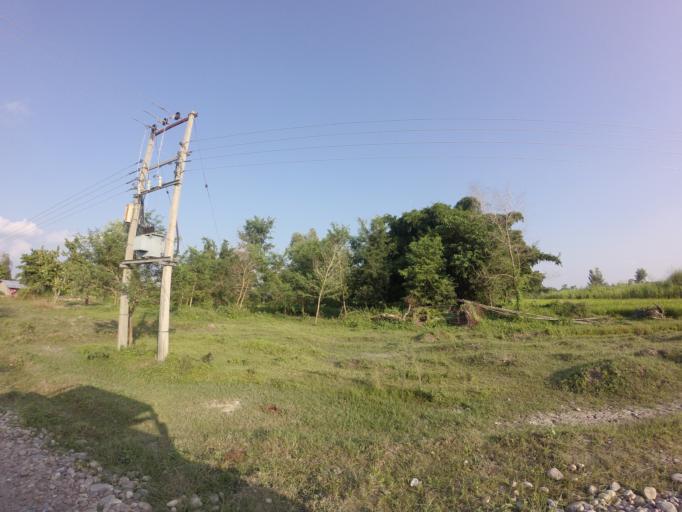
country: NP
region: Far Western
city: Tikapur
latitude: 28.4417
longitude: 81.0707
